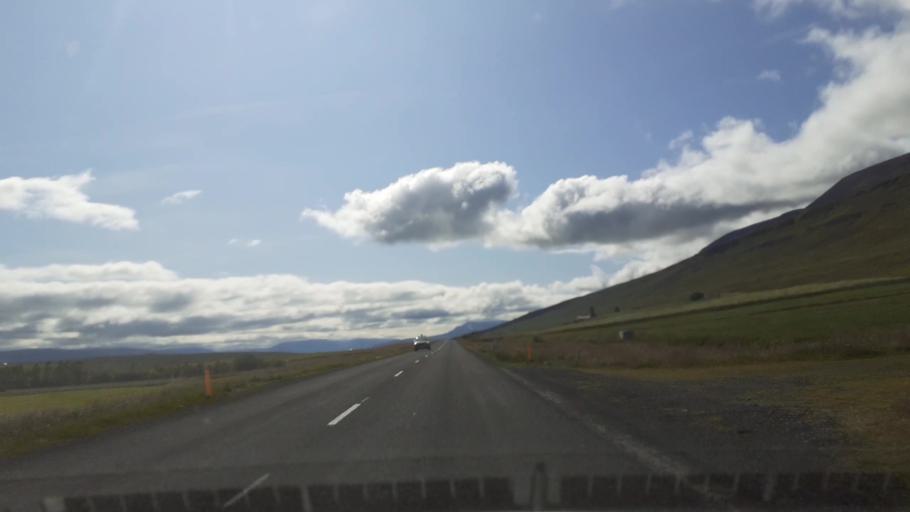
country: IS
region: Northeast
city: Akureyri
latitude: 65.8643
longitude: -18.2615
